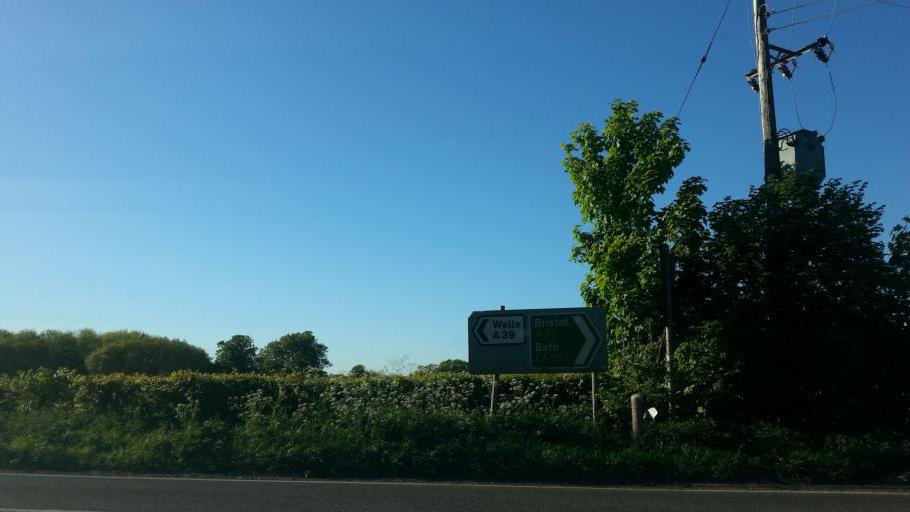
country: GB
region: England
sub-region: Bath and North East Somerset
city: Cameley
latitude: 51.2926
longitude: -2.5396
